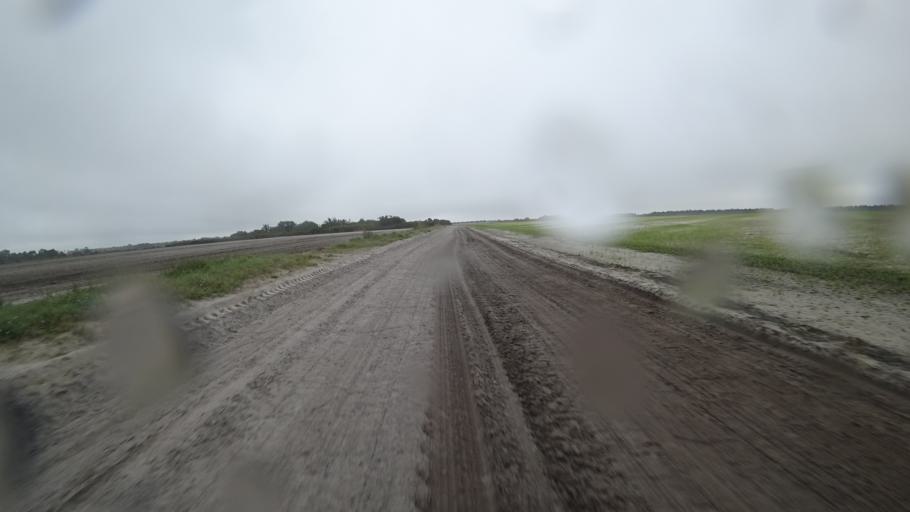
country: US
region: Florida
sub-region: Sarasota County
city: Warm Mineral Springs
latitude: 27.2998
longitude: -82.1643
